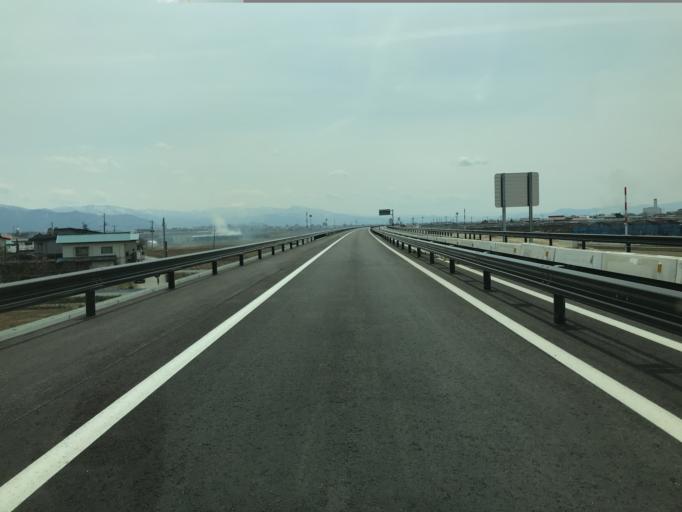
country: JP
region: Yamagata
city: Higashine
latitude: 38.4427
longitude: 140.3538
